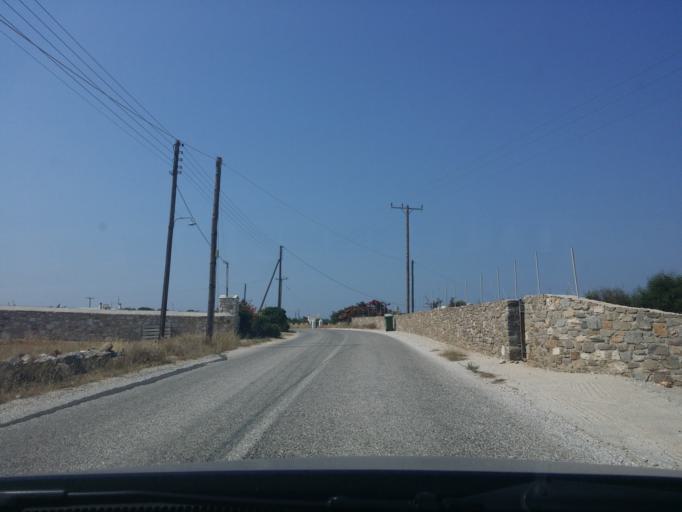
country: GR
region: South Aegean
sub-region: Nomos Kykladon
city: Antiparos
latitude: 37.0295
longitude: 25.1095
